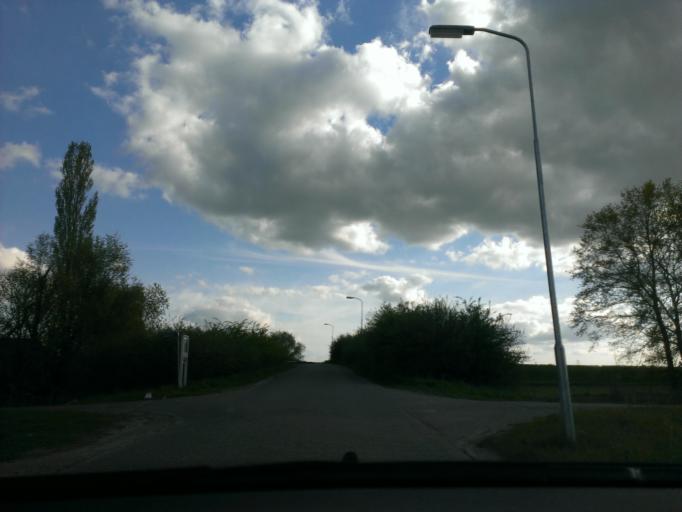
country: NL
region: Gelderland
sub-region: Gemeente Heerde
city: Heerde
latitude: 52.3761
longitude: 6.0835
